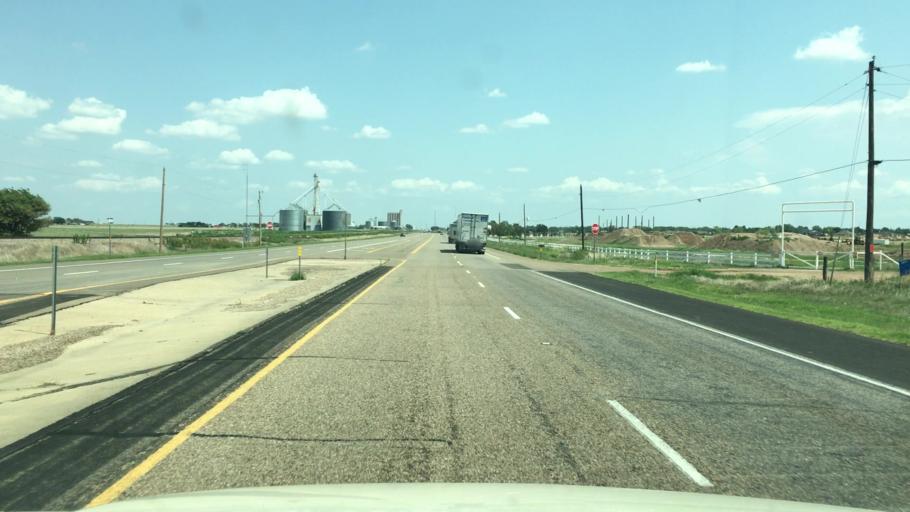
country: US
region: Texas
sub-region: Armstrong County
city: Claude
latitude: 35.1195
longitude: -101.3816
